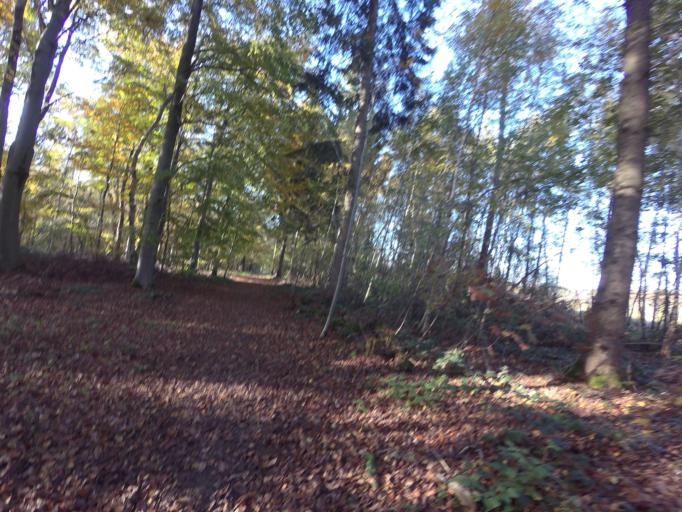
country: NL
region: Limburg
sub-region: Gemeente Simpelveld
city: Simpelveld
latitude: 50.8048
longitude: 5.9727
